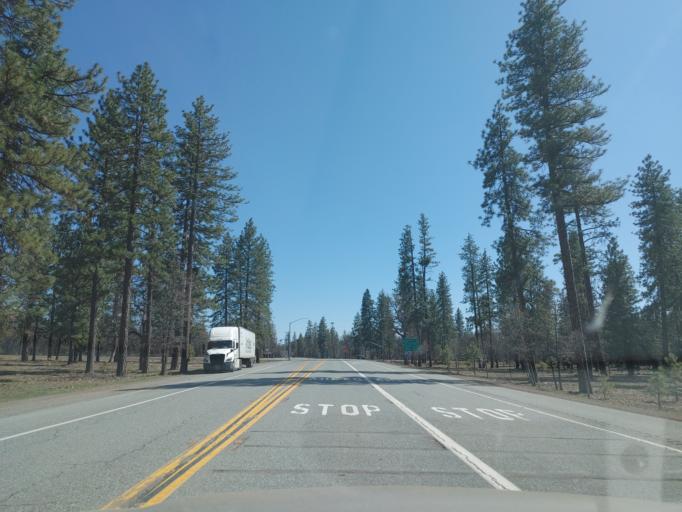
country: US
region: California
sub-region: Shasta County
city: Burney
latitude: 40.9398
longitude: -121.6073
